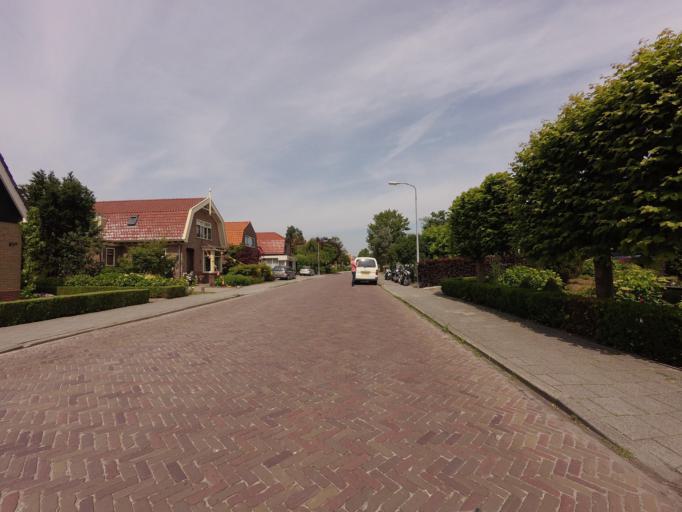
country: NL
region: North Holland
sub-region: Gemeente Hoorn
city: Hoorn
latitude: 52.6868
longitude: 5.0193
